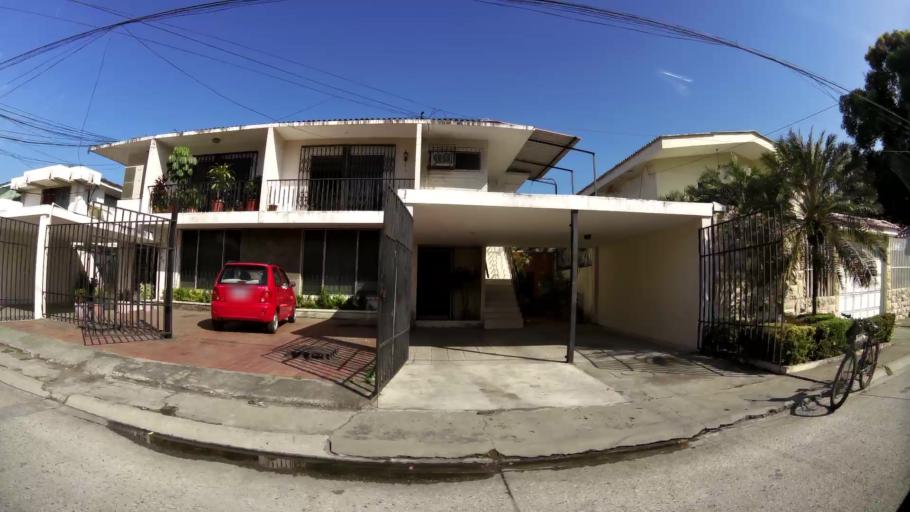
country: EC
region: Guayas
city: Guayaquil
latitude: -2.1693
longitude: -79.9043
